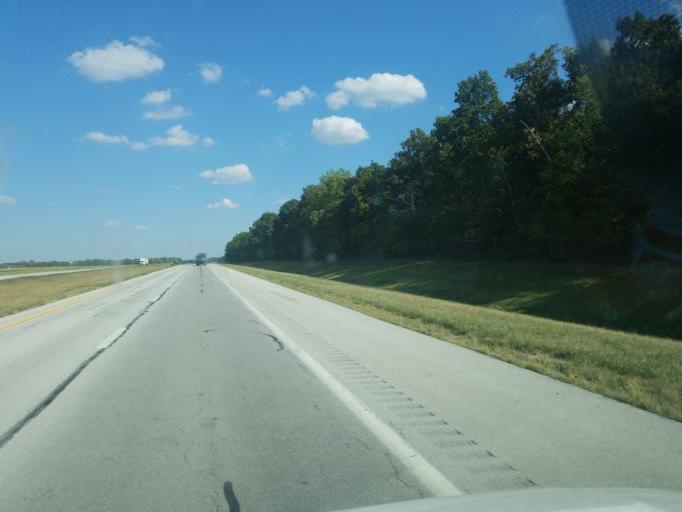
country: US
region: Ohio
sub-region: Wyandot County
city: Upper Sandusky
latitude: 40.8252
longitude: -83.3746
